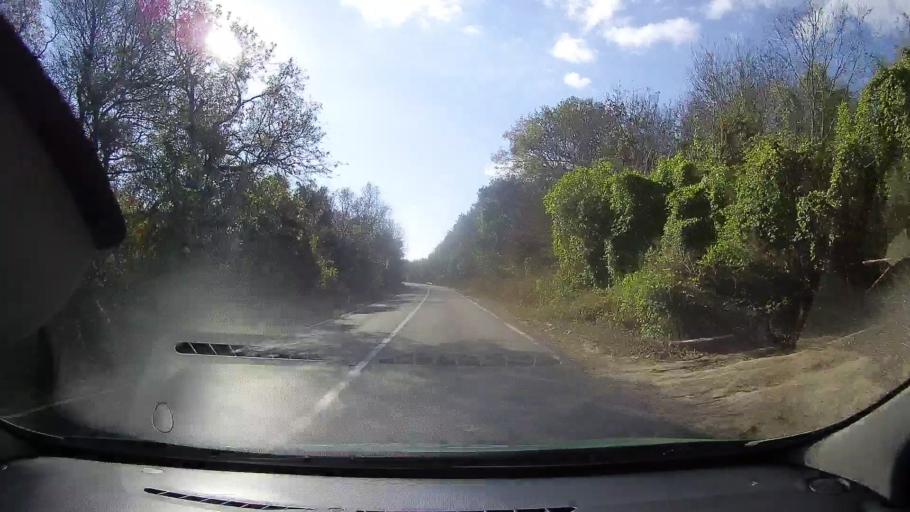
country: RO
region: Tulcea
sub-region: Oras Babadag
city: Babadag
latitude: 44.8399
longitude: 28.6964
